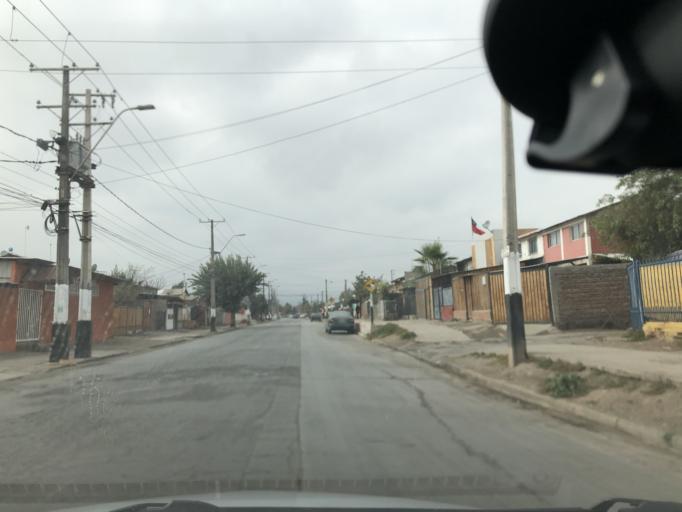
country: CL
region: Santiago Metropolitan
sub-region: Provincia de Santiago
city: La Pintana
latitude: -33.5891
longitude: -70.6068
